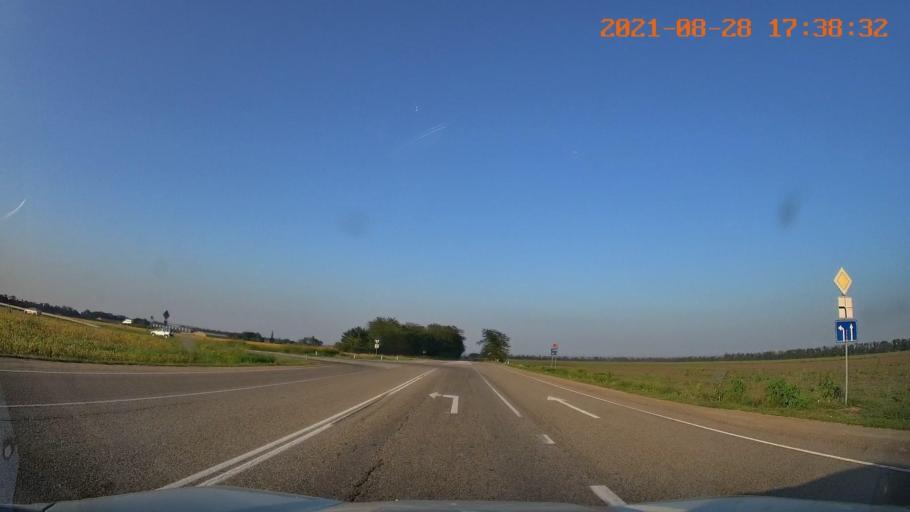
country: RU
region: Krasnodarskiy
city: Novokubansk
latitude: 45.0596
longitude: 40.9872
